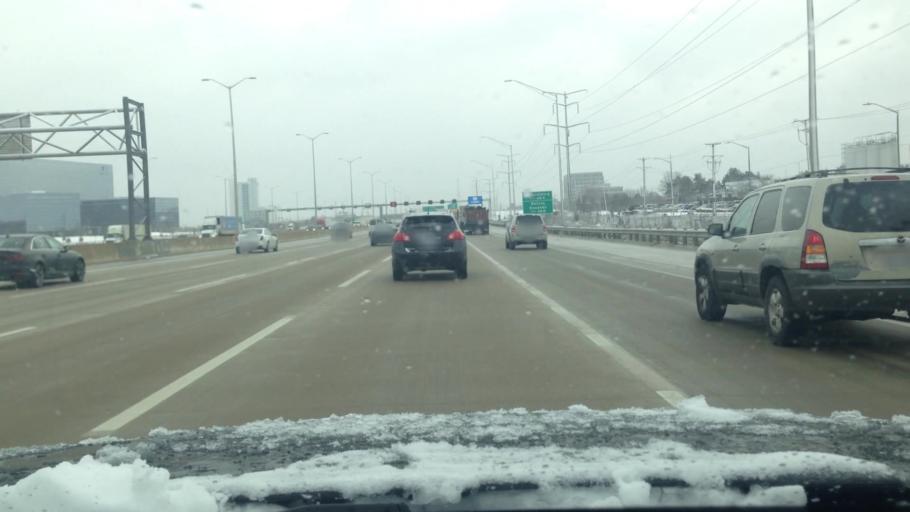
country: US
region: Illinois
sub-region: Cook County
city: Hoffman Estates
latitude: 42.0606
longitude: -88.0544
